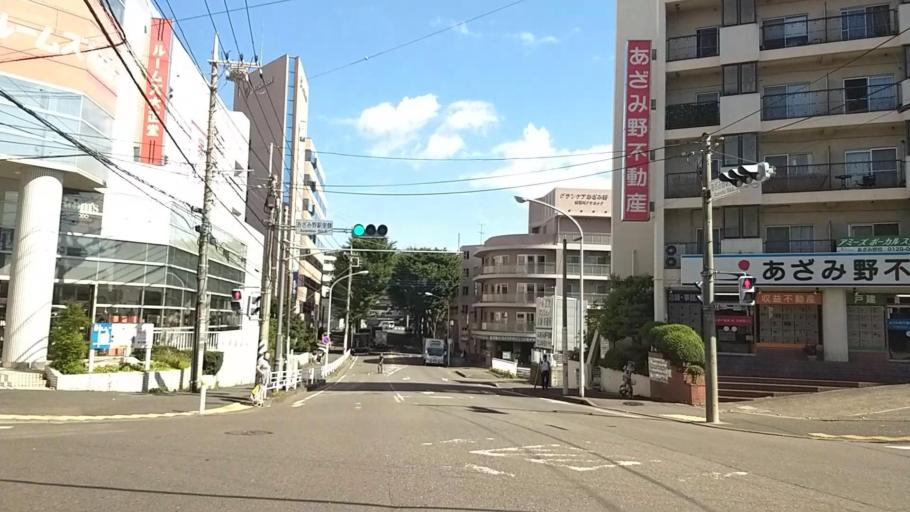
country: JP
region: Tokyo
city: Chofugaoka
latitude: 35.5688
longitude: 139.5543
